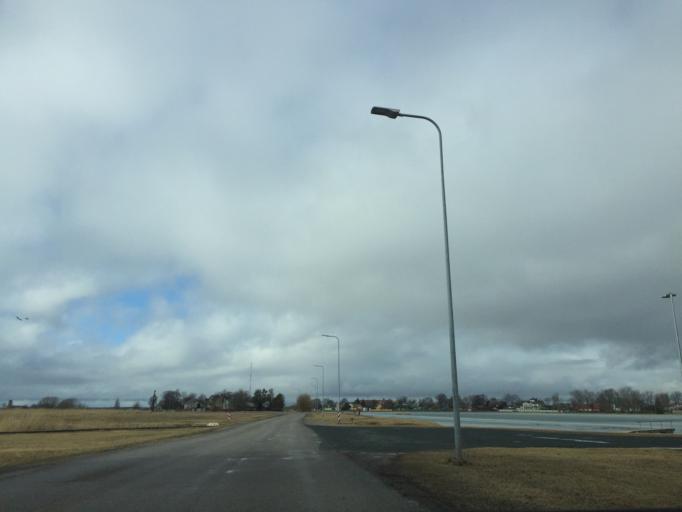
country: EE
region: Laeaene
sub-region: Haapsalu linn
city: Haapsalu
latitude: 58.9498
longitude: 23.5275
